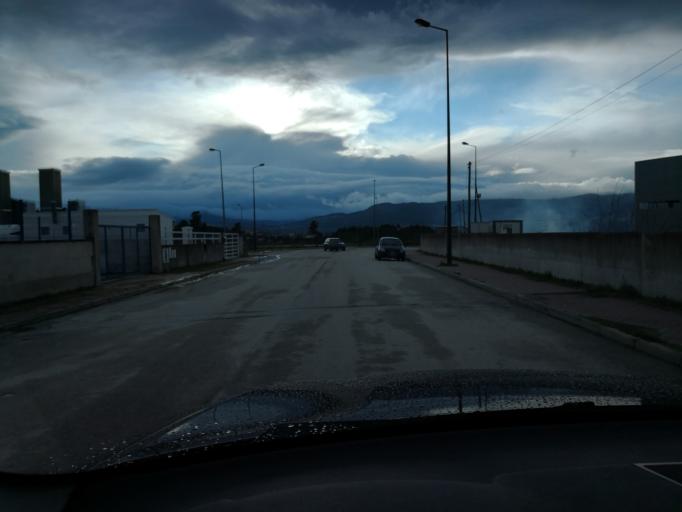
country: PT
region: Vila Real
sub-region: Vila Real
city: Vila Real
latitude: 41.2808
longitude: -7.7113
